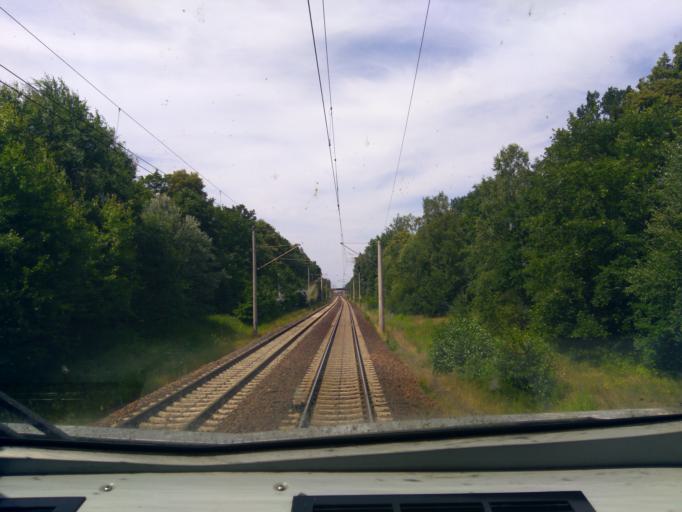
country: DE
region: Brandenburg
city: Brieselang
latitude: 52.5765
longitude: 13.0253
